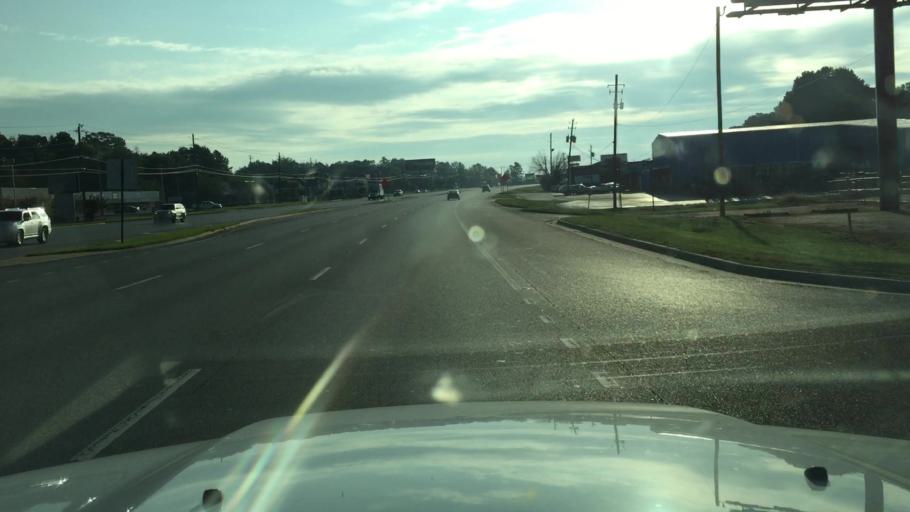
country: US
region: Alabama
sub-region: Tuscaloosa County
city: Northport
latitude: 33.2407
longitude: -87.5884
